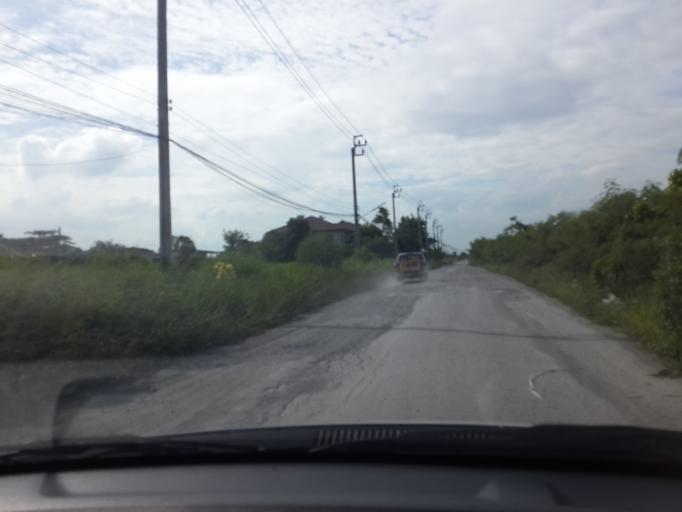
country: TH
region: Bangkok
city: Nong Chok
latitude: 13.8531
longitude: 100.8006
